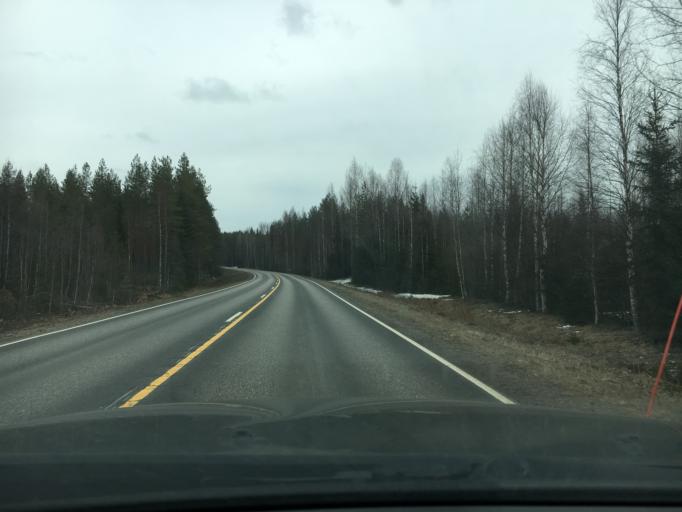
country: FI
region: Central Finland
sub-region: AEaenekoski
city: Sumiainen
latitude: 62.5541
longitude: 26.0010
